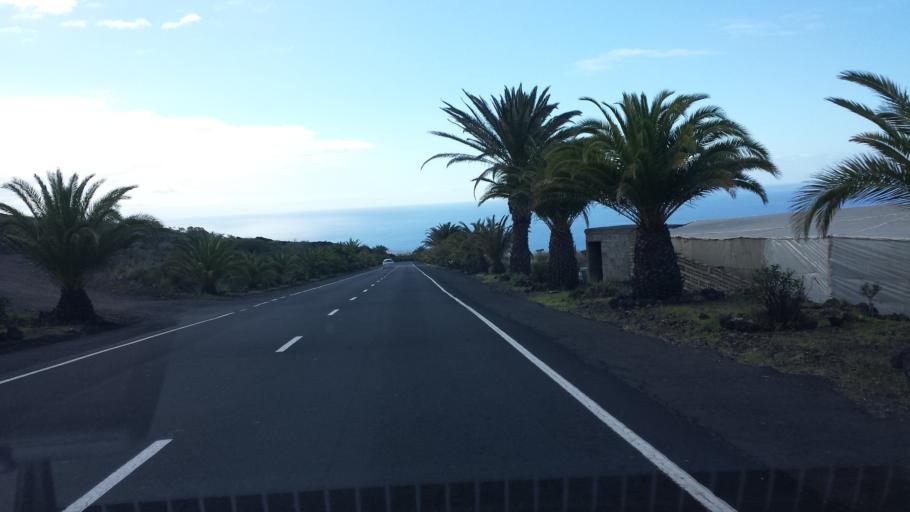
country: ES
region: Canary Islands
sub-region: Provincia de Santa Cruz de Tenerife
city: Tazacorte
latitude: 28.6041
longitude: -17.9078
